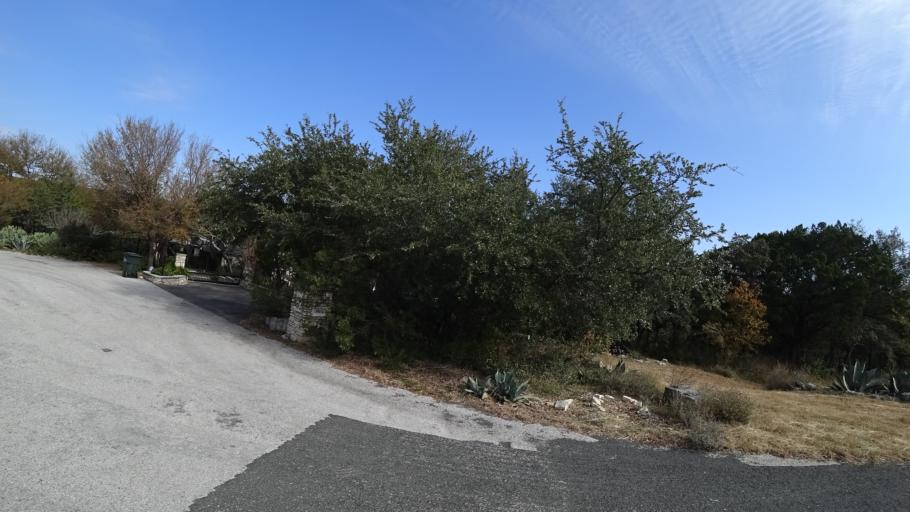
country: US
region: Texas
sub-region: Williamson County
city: Jollyville
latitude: 30.3796
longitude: -97.8161
